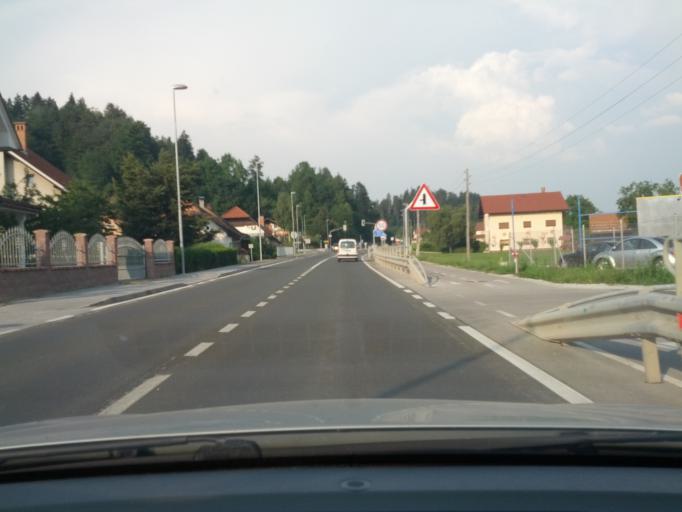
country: SI
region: Log-Dragomer
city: Dragomer
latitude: 46.0169
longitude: 14.3854
